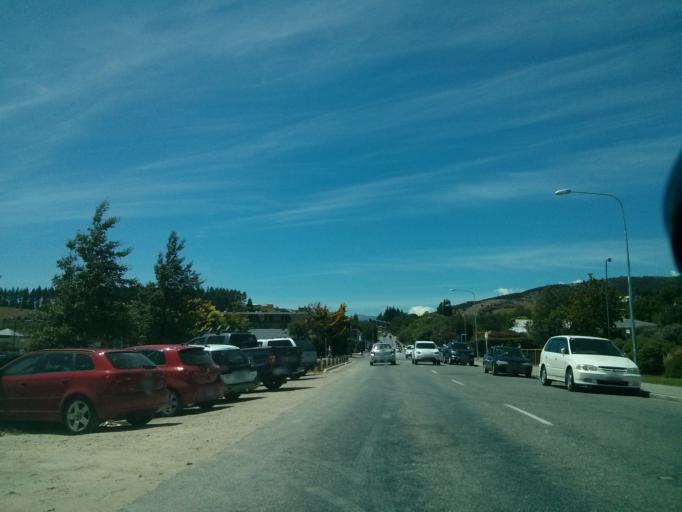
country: NZ
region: Otago
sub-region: Queenstown-Lakes District
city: Wanaka
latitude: -44.6981
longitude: 169.1339
